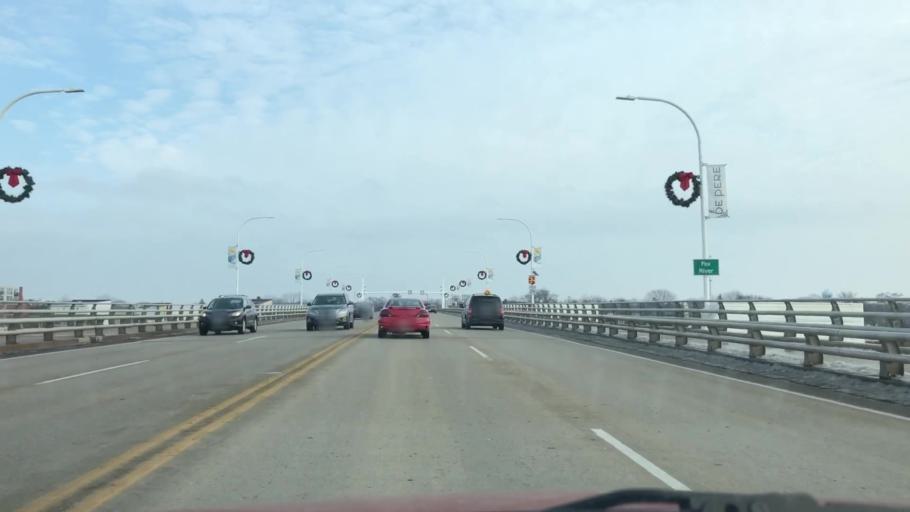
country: US
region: Wisconsin
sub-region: Brown County
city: De Pere
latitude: 44.4476
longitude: -88.0643
